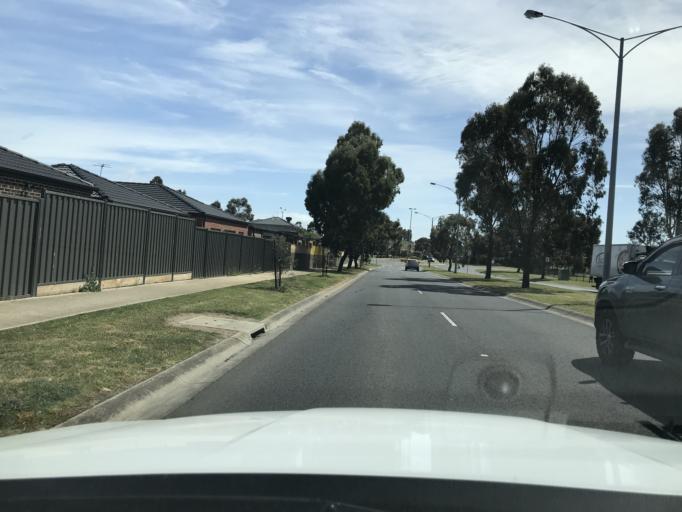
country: AU
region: Victoria
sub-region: Hume
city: Roxburgh Park
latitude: -37.6214
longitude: 144.9323
